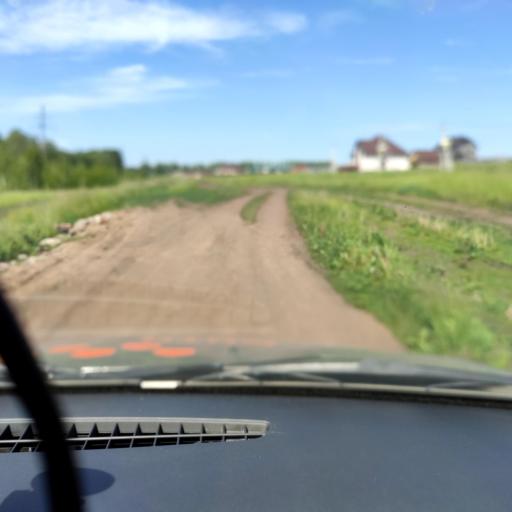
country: RU
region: Bashkortostan
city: Ufa
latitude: 54.6835
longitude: 56.0868
